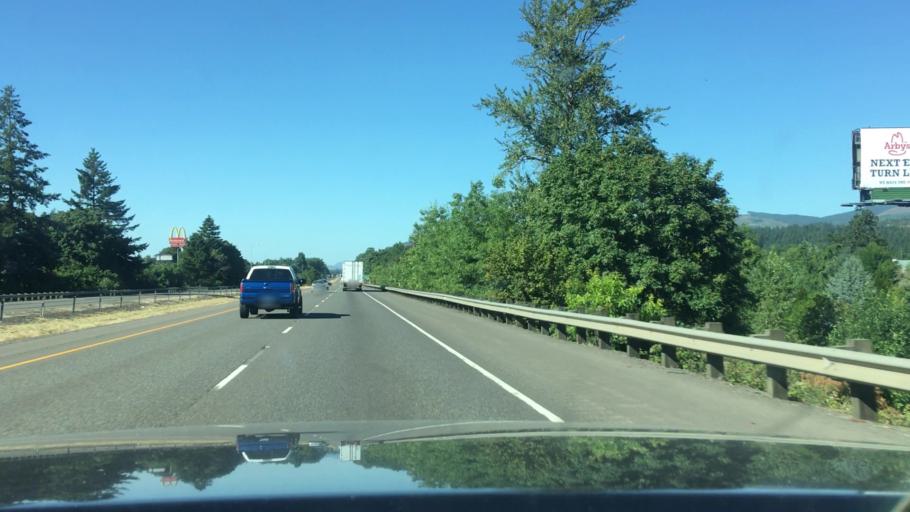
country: US
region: Oregon
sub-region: Lane County
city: Cottage Grove
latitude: 43.8012
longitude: -123.0443
